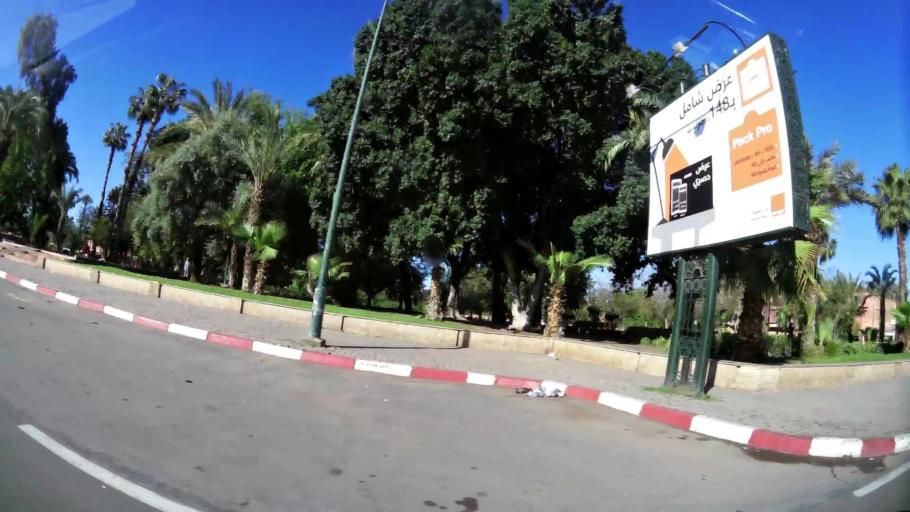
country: MA
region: Marrakech-Tensift-Al Haouz
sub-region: Marrakech
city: Marrakesh
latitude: 31.6351
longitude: -8.0000
